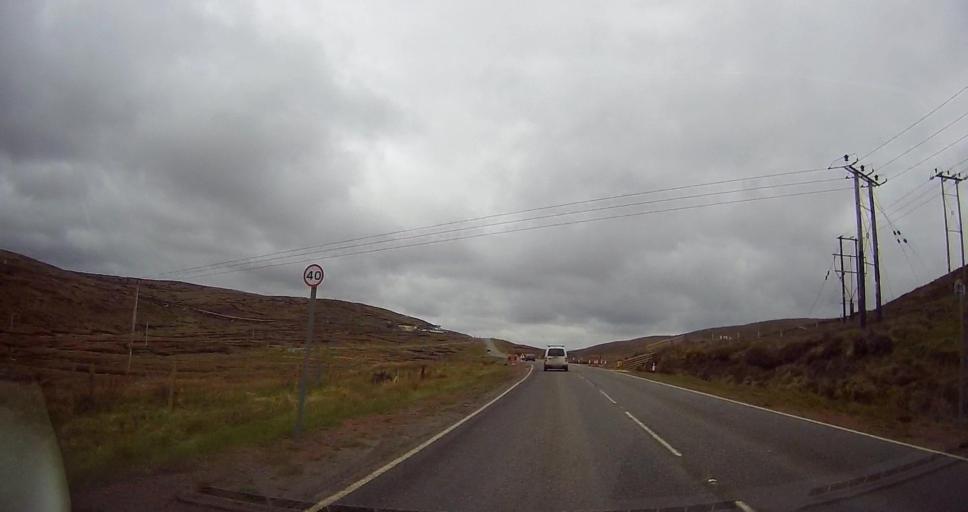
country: GB
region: Scotland
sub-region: Shetland Islands
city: Lerwick
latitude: 60.3313
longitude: -1.2539
